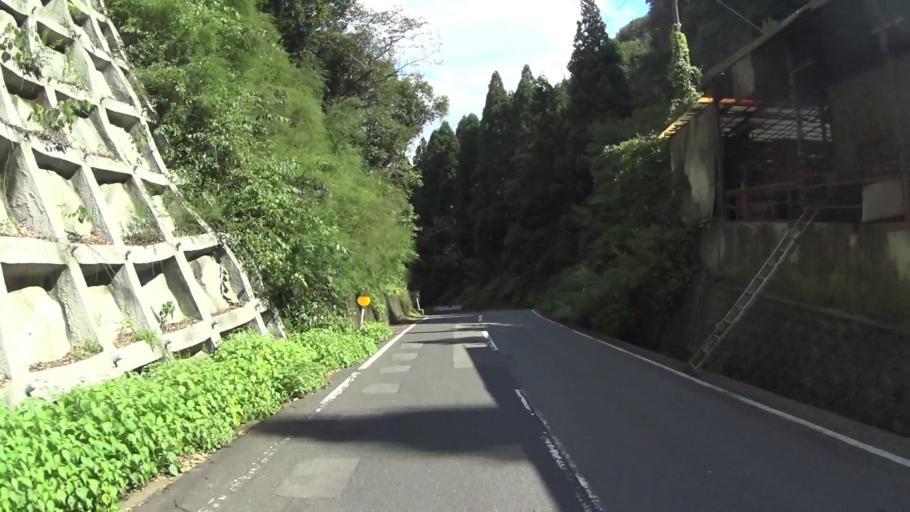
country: JP
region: Kyoto
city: Uji
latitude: 34.9098
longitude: 135.8625
